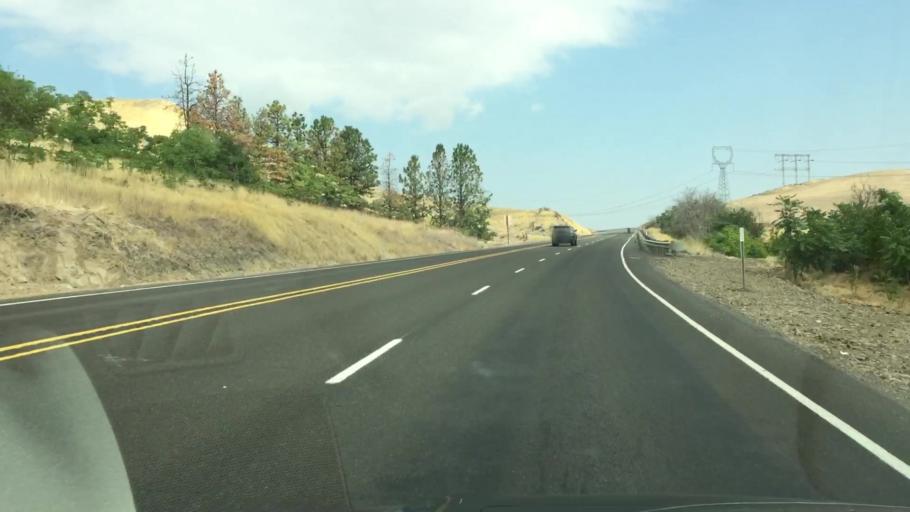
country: US
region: Oregon
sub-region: Wasco County
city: The Dalles
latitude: 45.5706
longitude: -121.1050
